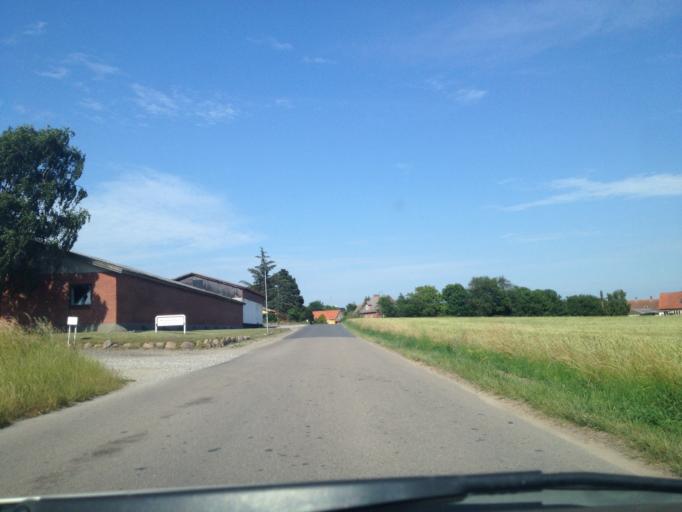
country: DK
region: Central Jutland
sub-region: Samso Kommune
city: Tranebjerg
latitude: 55.8483
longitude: 10.5677
